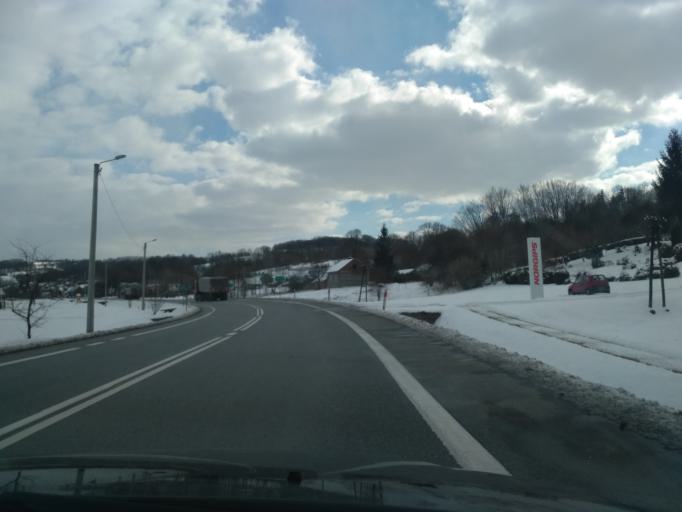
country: PL
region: Subcarpathian Voivodeship
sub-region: Powiat strzyzowski
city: Polomia
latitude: 49.9071
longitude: 21.8658
